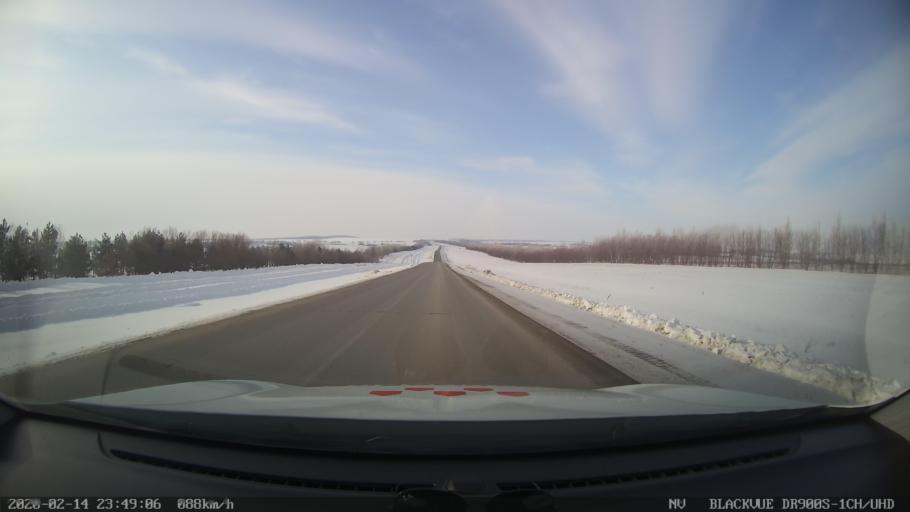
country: RU
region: Tatarstan
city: Kuybyshevskiy Zaton
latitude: 55.2515
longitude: 49.1896
